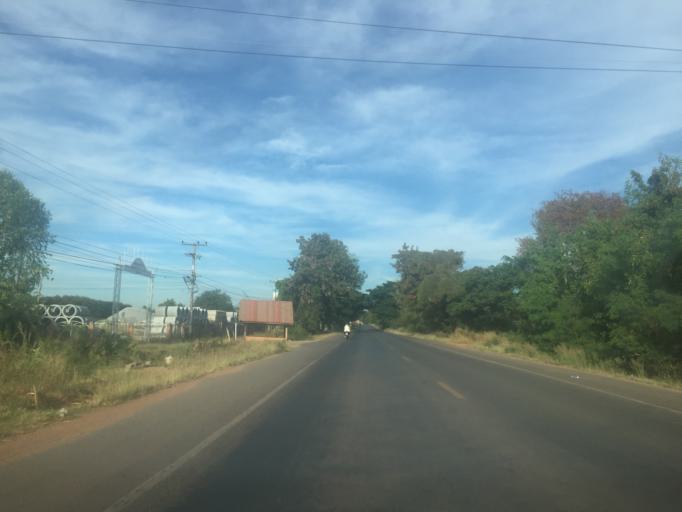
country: TH
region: Changwat Udon Thani
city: Si That
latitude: 16.9717
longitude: 103.2331
